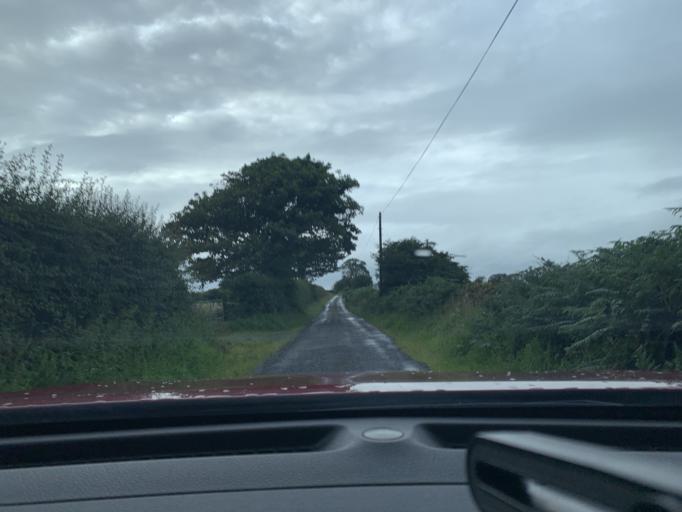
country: IE
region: Connaught
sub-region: Sligo
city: Strandhill
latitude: 54.3595
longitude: -8.5514
